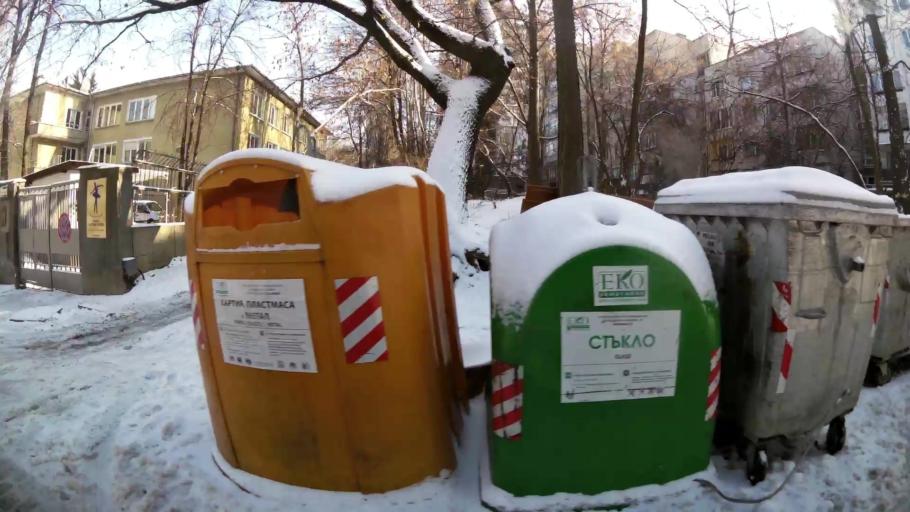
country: BG
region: Sofia-Capital
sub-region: Stolichna Obshtina
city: Sofia
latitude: 42.6772
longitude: 23.3270
